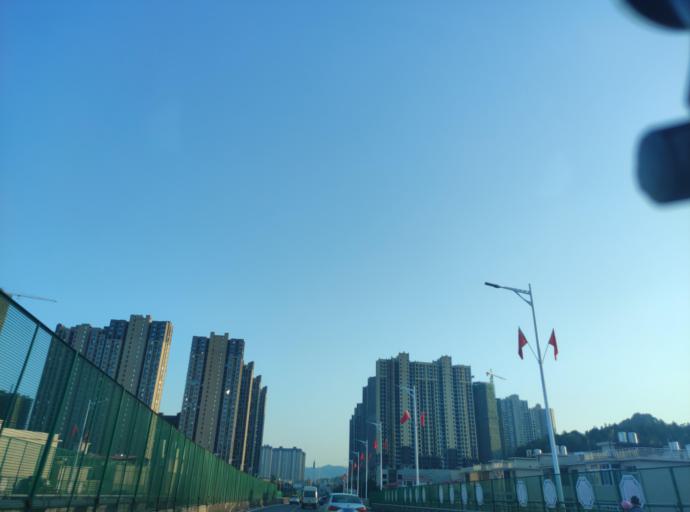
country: CN
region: Jiangxi Sheng
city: Pingxiang
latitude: 27.6386
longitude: 113.8296
